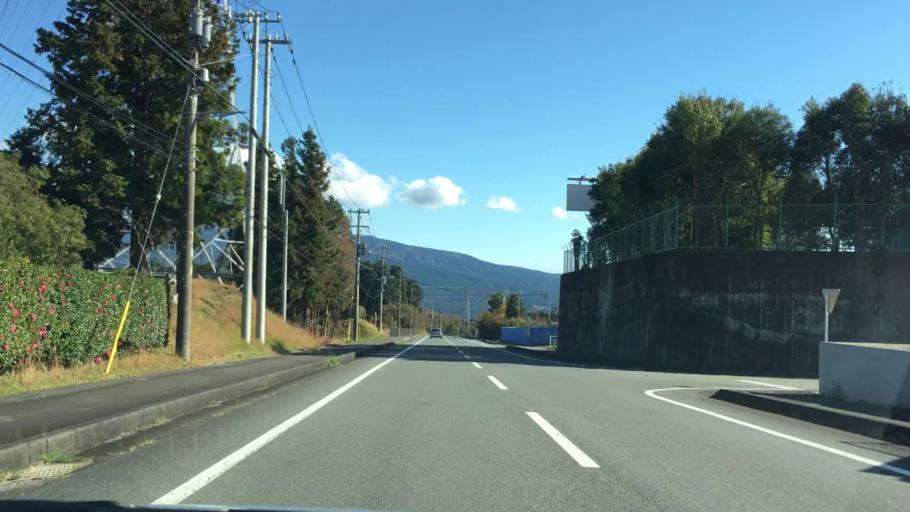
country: JP
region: Shizuoka
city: Gotemba
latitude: 35.2269
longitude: 138.8892
